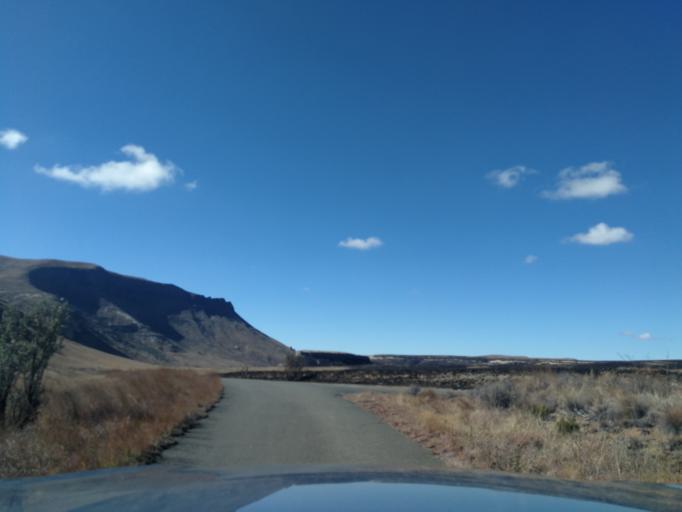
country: ZA
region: Orange Free State
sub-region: Thabo Mofutsanyana District Municipality
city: Phuthaditjhaba
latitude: -28.5136
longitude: 28.6182
